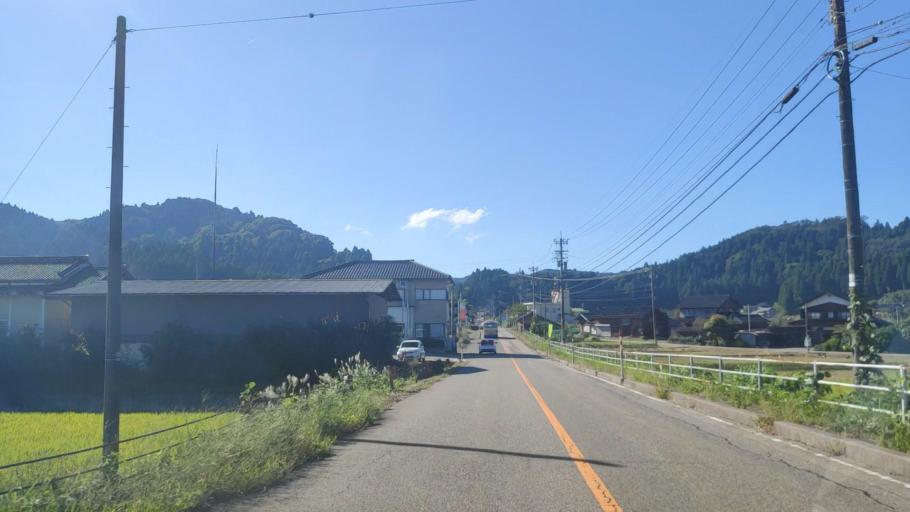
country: JP
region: Ishikawa
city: Nanao
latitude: 37.2807
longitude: 137.0443
